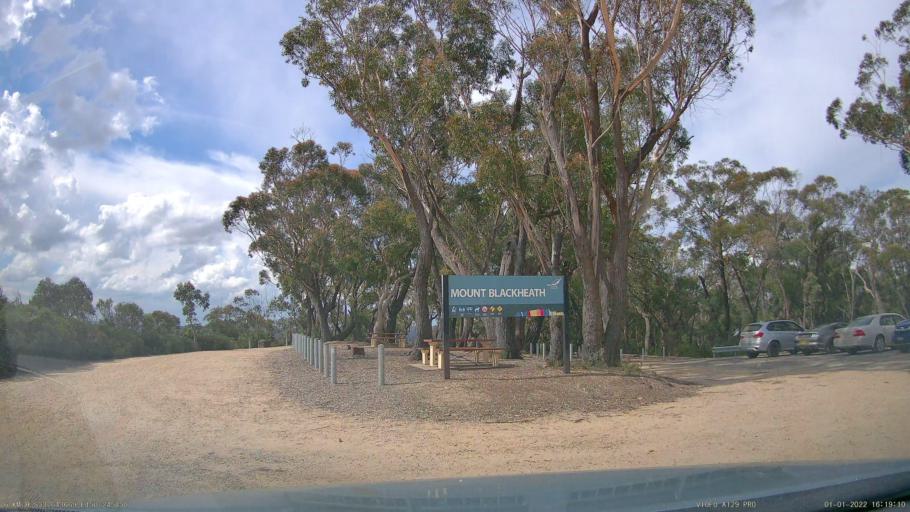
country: AU
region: New South Wales
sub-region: Blue Mountains Municipality
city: Blackheath
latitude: -33.6437
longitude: 150.2451
